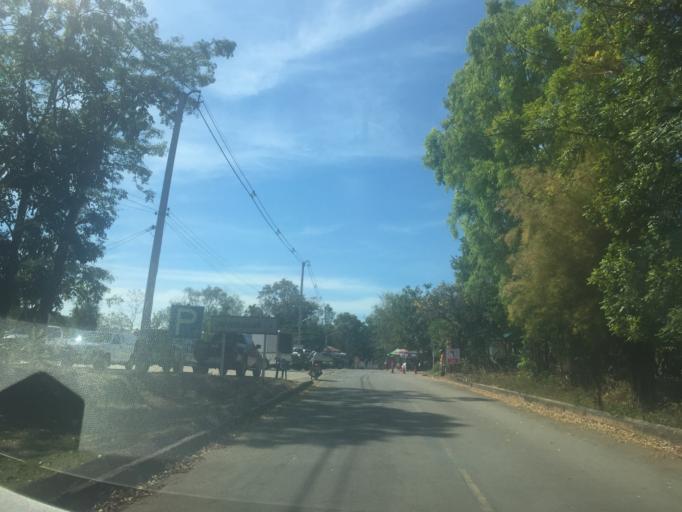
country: TH
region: Changwat Nong Bua Lamphu
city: Nong Bua Lamphu
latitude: 17.2447
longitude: 102.5156
